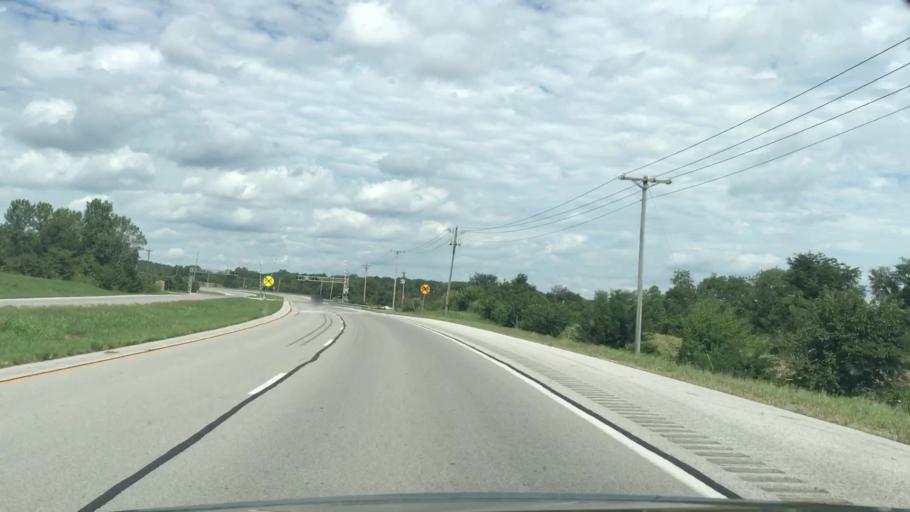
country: US
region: Kentucky
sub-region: Logan County
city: Russellville
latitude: 36.8607
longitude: -86.8630
